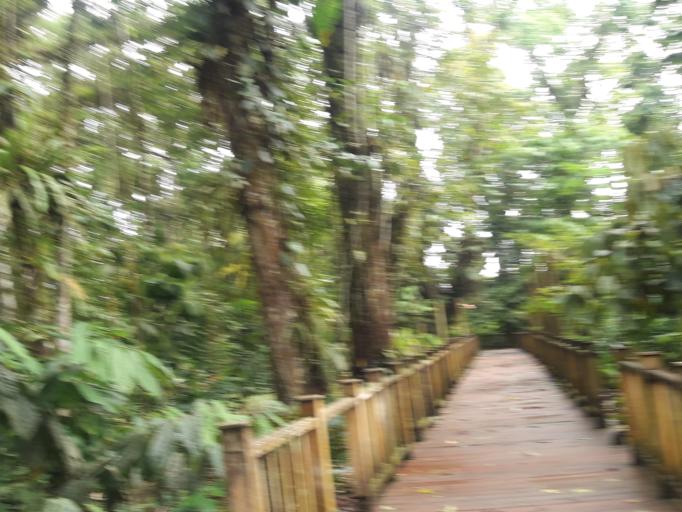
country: EC
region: Napo
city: Tena
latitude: -0.9949
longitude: -77.8152
